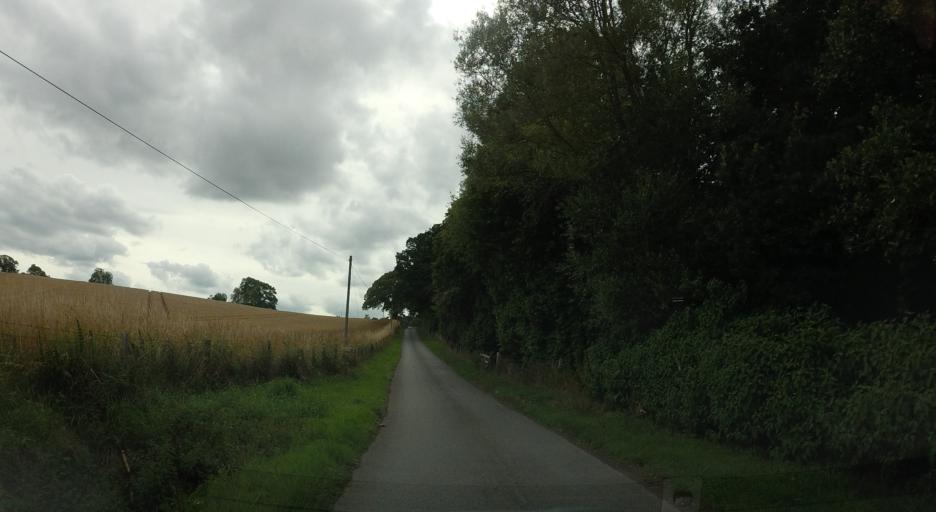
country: GB
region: Scotland
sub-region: Perth and Kinross
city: Bridge of Earn
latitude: 56.3697
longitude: -3.3587
